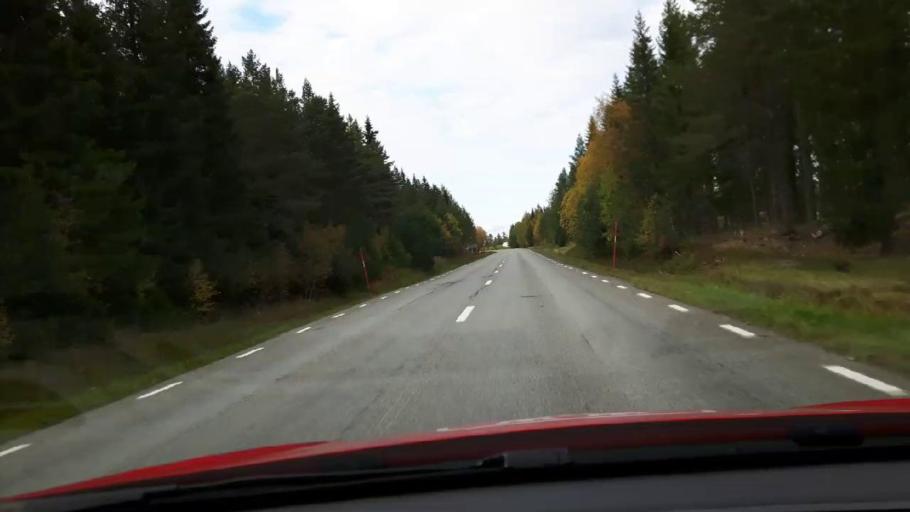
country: SE
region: Jaemtland
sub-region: Krokoms Kommun
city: Valla
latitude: 63.2332
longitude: 14.0105
